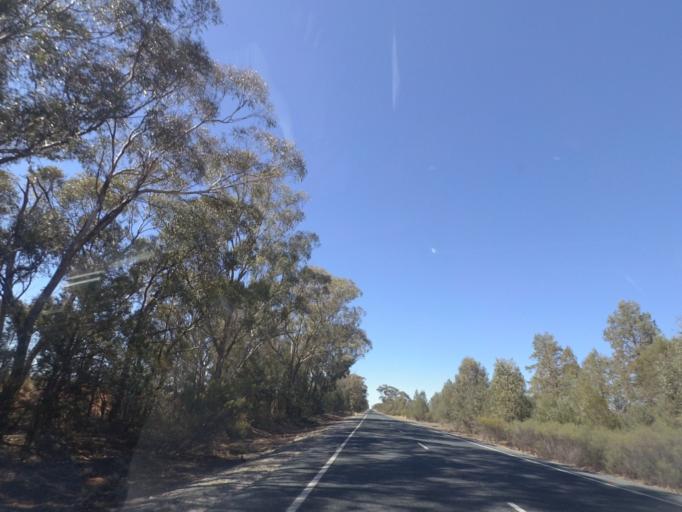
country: AU
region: New South Wales
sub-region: Bland
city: West Wyalong
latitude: -34.1516
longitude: 147.1184
